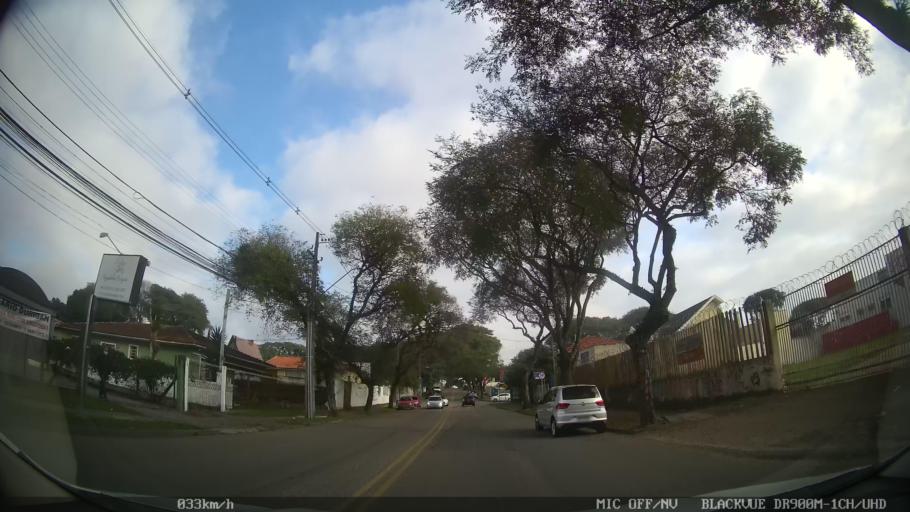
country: BR
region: Parana
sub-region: Curitiba
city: Curitiba
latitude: -25.3980
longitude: -49.3377
